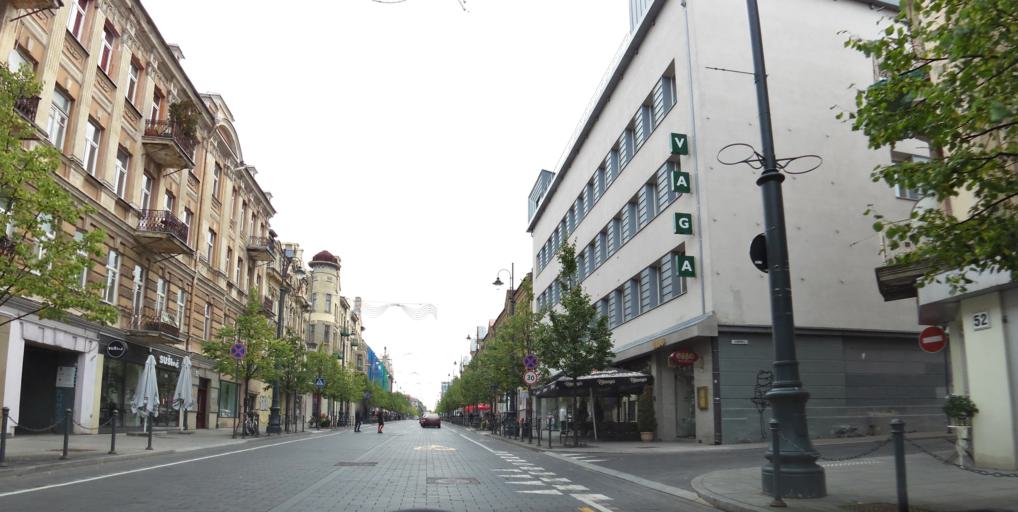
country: LT
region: Vilnius County
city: Naujamiestis
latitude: 54.6896
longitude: 25.2657
